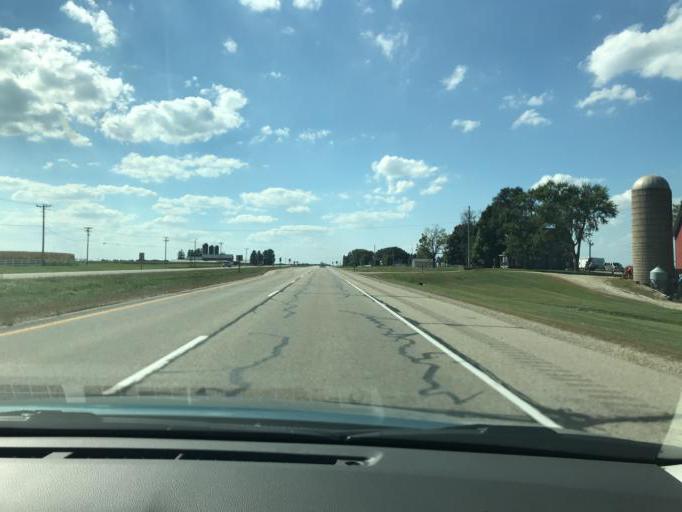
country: US
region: Wisconsin
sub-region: Kenosha County
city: Powers Lake
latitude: 42.5816
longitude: -88.3128
